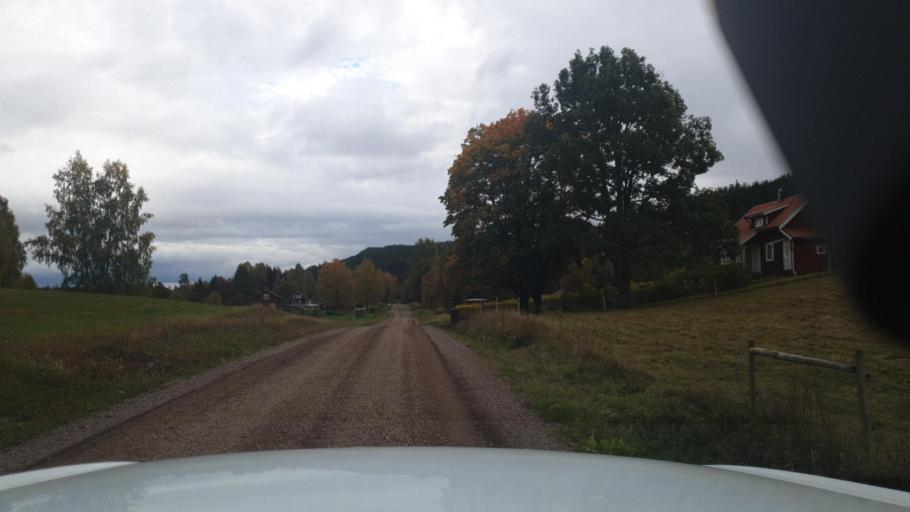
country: SE
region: Vaermland
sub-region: Eda Kommun
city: Charlottenberg
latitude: 60.0747
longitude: 12.5278
